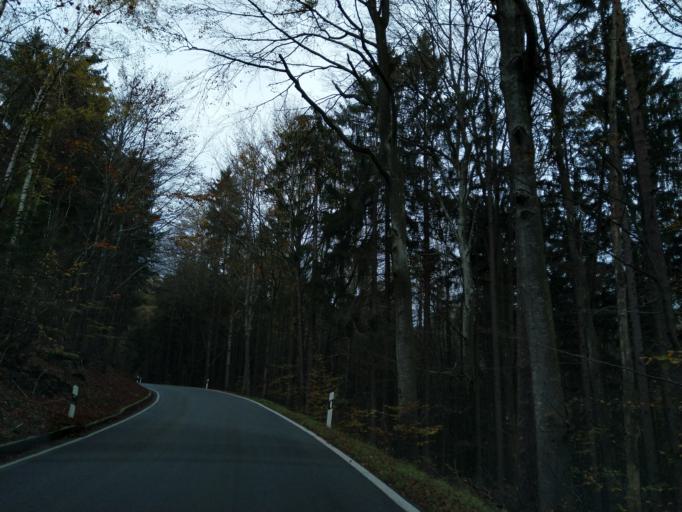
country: DE
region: Bavaria
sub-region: Lower Bavaria
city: Zenting
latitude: 48.8011
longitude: 13.2325
